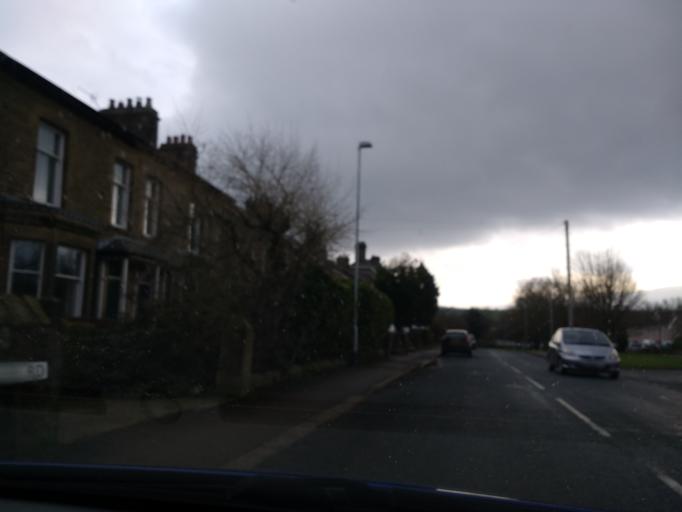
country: GB
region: England
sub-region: Lancashire
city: Caton
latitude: 54.0745
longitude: -2.7159
